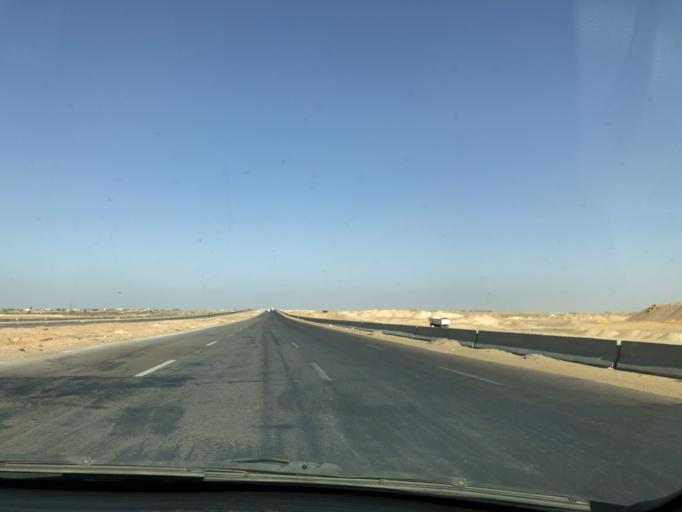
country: EG
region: Muhafazat al Minufiyah
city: Ashmun
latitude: 30.0674
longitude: 30.8553
